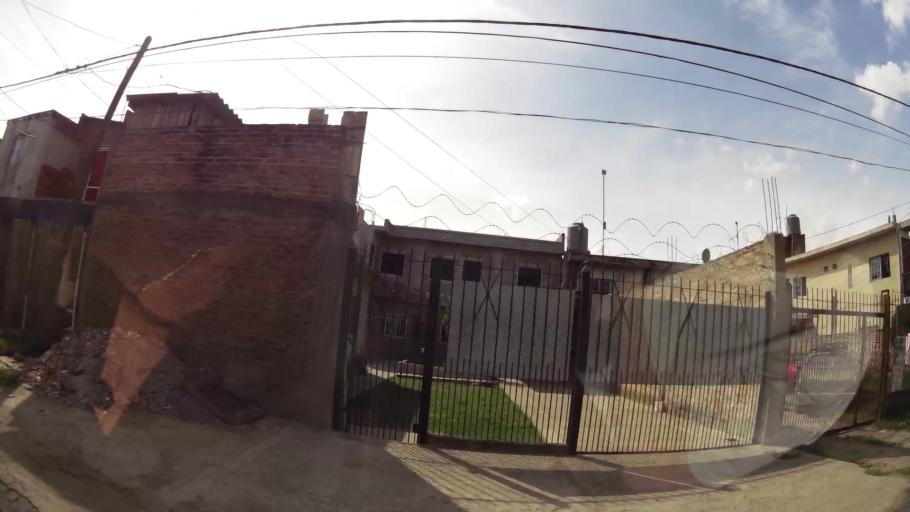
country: AR
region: Buenos Aires
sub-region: Partido de Quilmes
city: Quilmes
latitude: -34.7621
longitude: -58.2497
